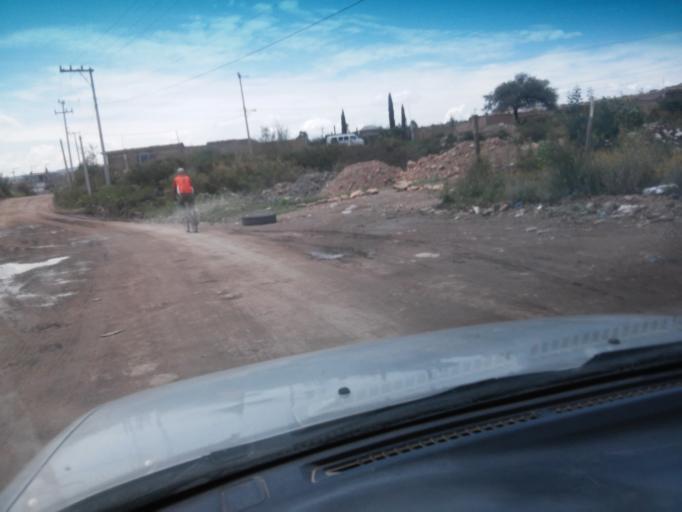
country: MX
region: Durango
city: Victoria de Durango
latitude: 23.9881
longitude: -104.7106
